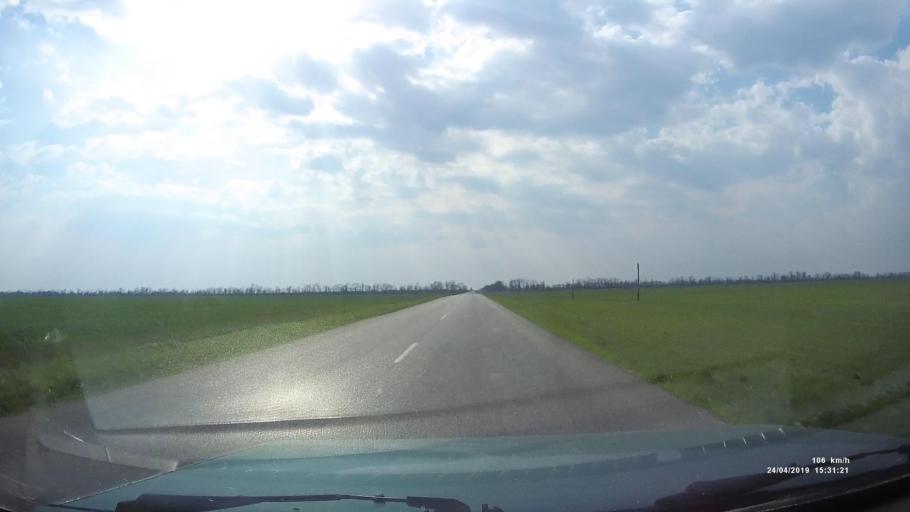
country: RU
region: Rostov
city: Remontnoye
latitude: 46.5997
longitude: 42.9854
